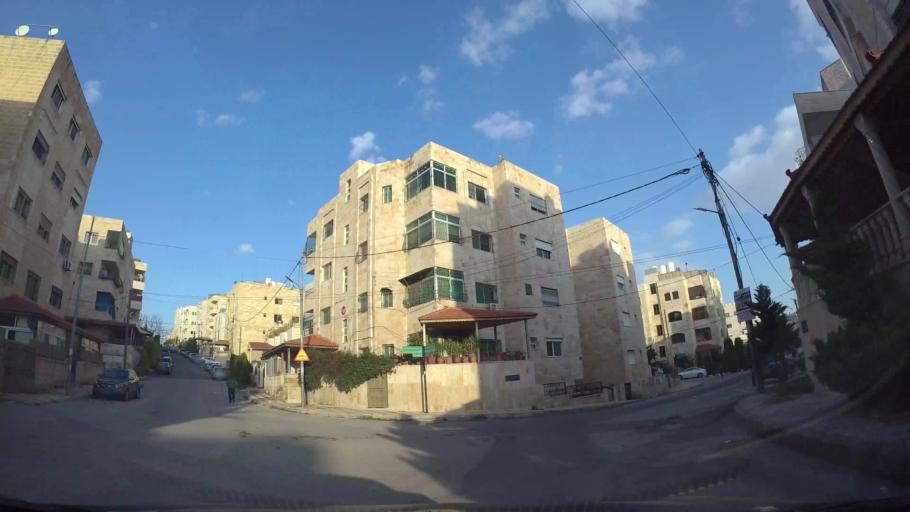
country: JO
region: Amman
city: Al Bunayyat ash Shamaliyah
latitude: 31.9130
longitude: 35.8904
